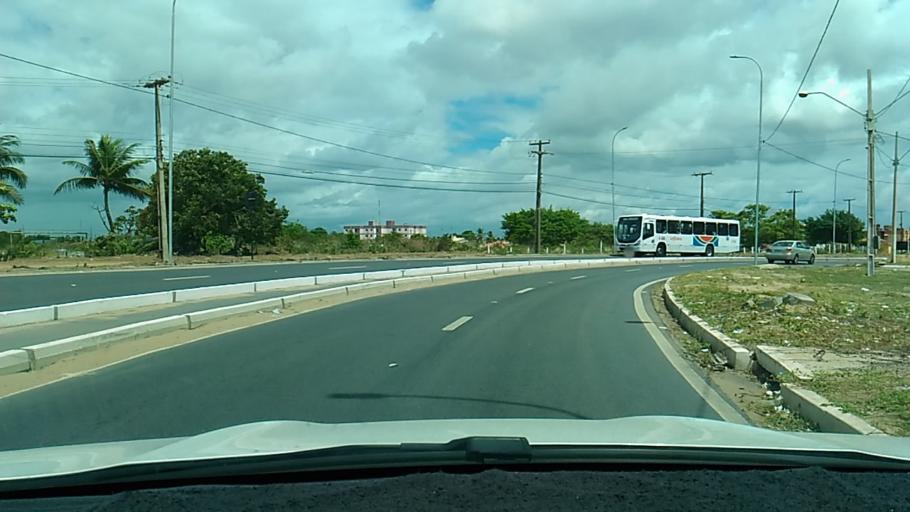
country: BR
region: Paraiba
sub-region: Joao Pessoa
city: Joao Pessoa
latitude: -7.1675
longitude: -34.8752
